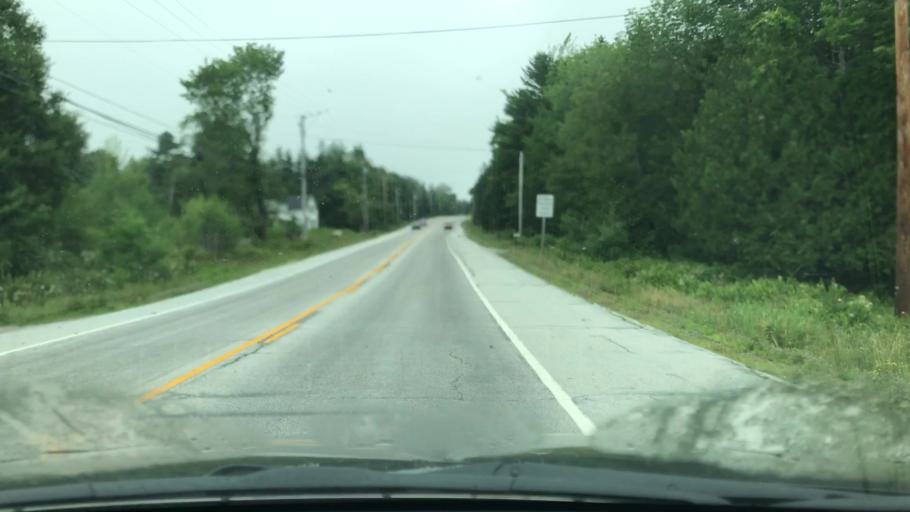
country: US
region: Maine
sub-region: Waldo County
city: Northport
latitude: 44.3061
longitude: -68.9763
